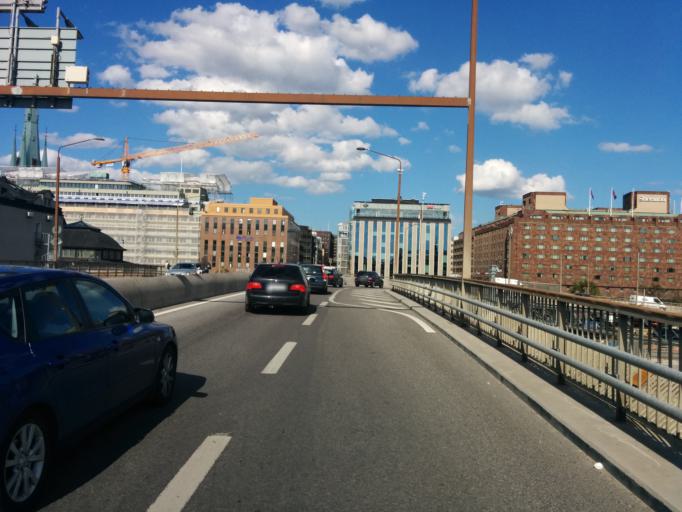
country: SE
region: Stockholm
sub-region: Stockholms Kommun
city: Stockholm
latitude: 59.3289
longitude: 18.0577
